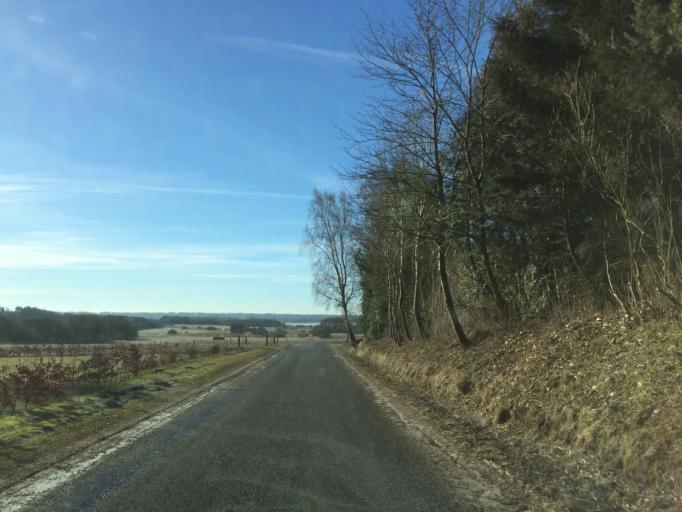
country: DK
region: North Denmark
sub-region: Mariagerfjord Kommune
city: Hobro
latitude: 56.6146
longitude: 9.6439
